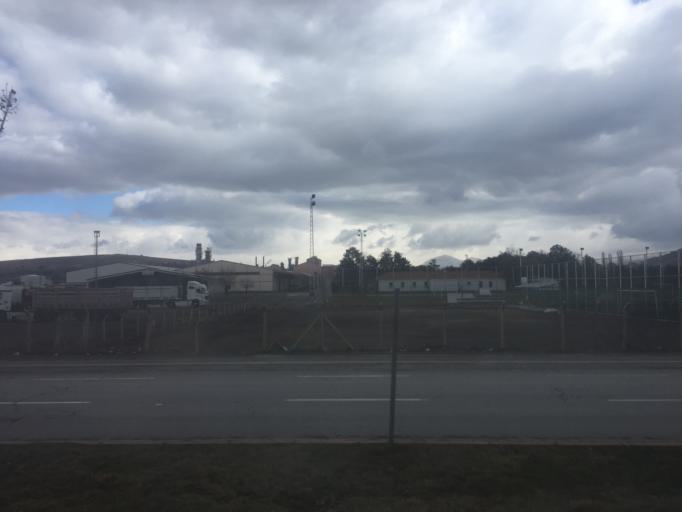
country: TR
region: Kayseri
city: Melikgazi
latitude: 38.7517
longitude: 35.4062
